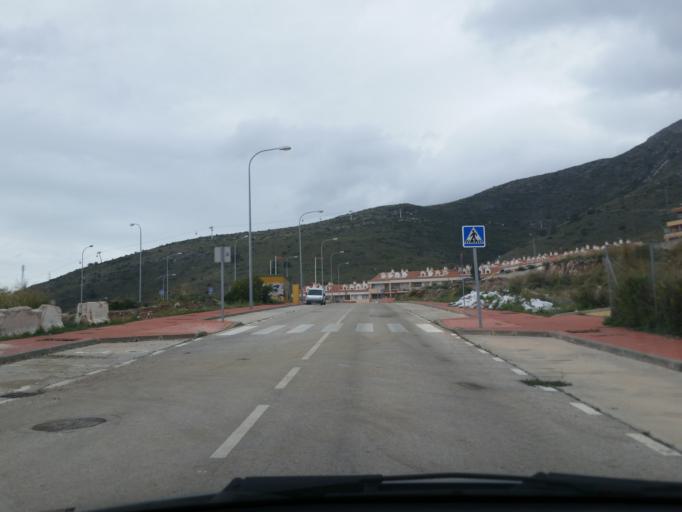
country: ES
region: Andalusia
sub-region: Provincia de Malaga
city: Benalmadena
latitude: 36.6130
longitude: -4.5437
